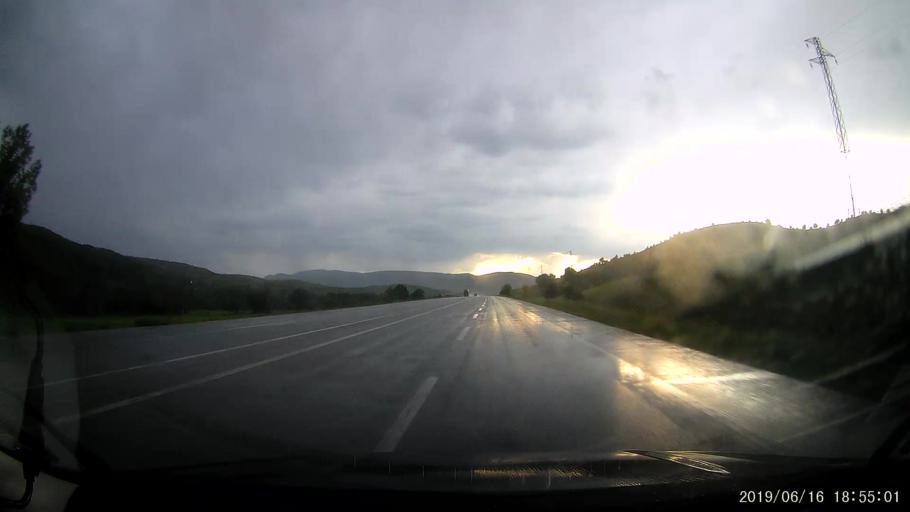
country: TR
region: Erzincan
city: Refahiye
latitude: 39.8987
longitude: 38.8389
